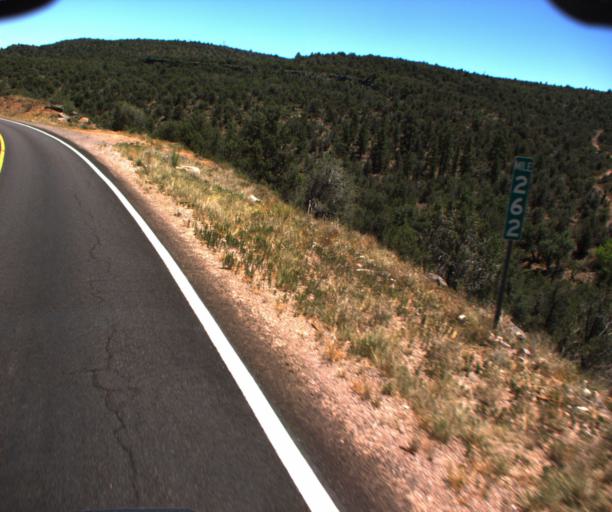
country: US
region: Arizona
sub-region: Gila County
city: Pine
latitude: 34.3197
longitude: -111.4148
